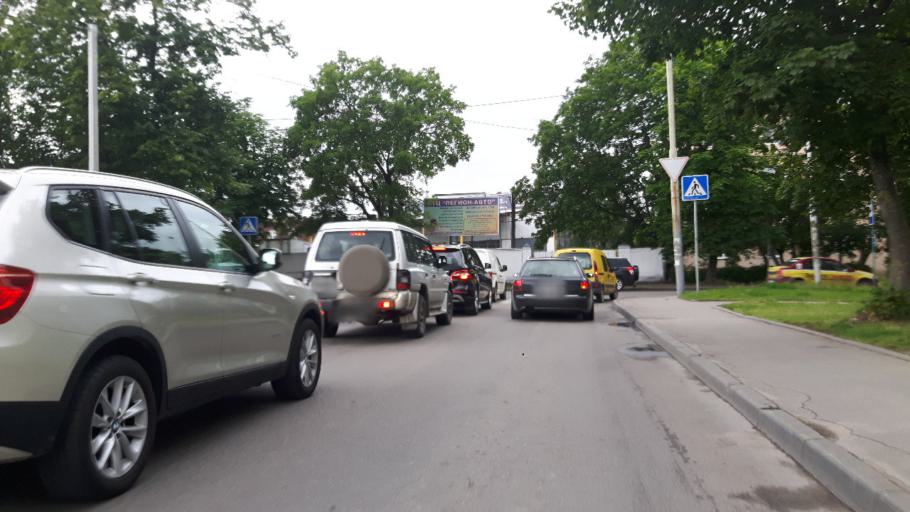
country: RU
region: Kaliningrad
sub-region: Gorod Kaliningrad
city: Kaliningrad
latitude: 54.7352
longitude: 20.4980
